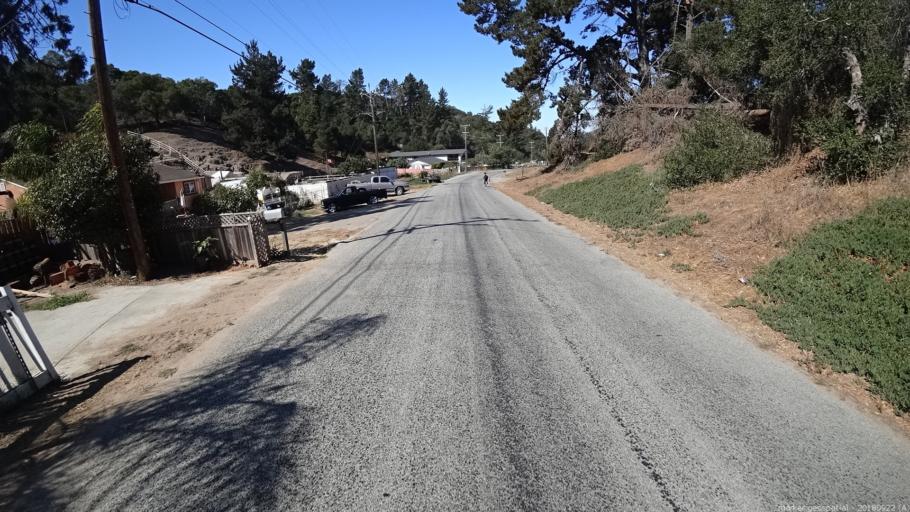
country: US
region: California
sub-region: Monterey County
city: Prunedale
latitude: 36.8109
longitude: -121.6356
